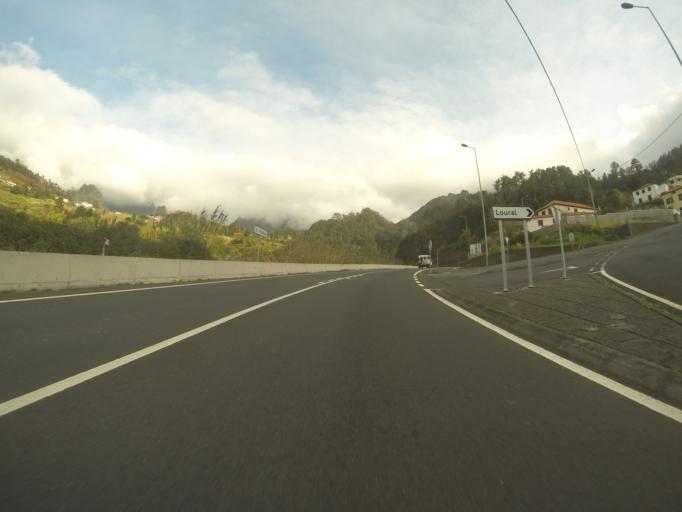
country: PT
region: Madeira
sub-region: Sao Vicente
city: Sao Vicente
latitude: 32.7744
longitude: -17.0314
